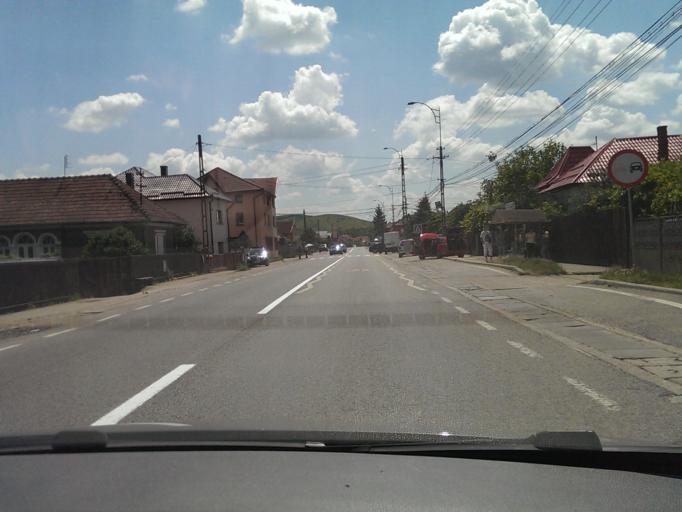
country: RO
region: Cluj
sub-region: Comuna Apahida
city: Apahida
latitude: 46.7968
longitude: 23.7508
